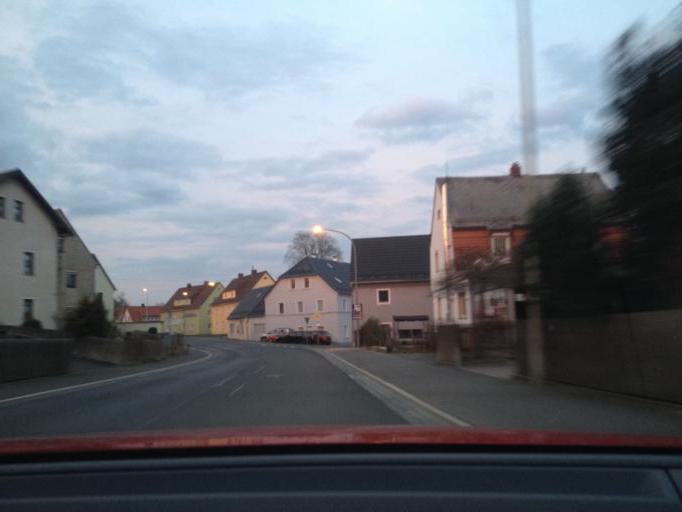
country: DE
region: Bavaria
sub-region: Upper Palatinate
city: Waldershof
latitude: 49.9785
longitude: 12.0661
